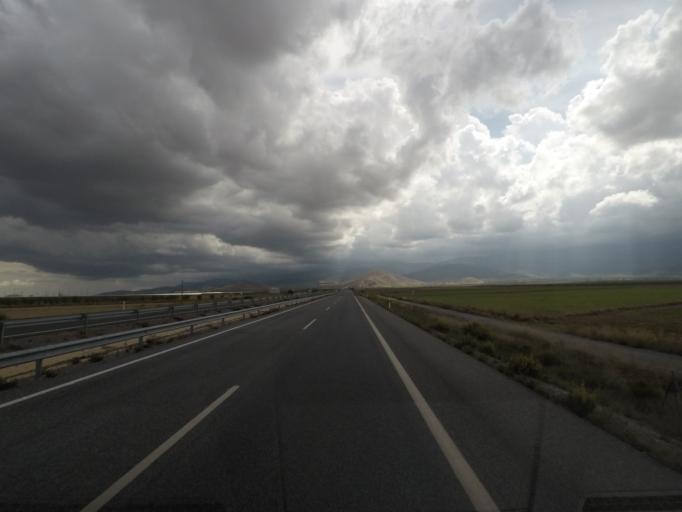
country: ES
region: Andalusia
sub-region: Provincia de Granada
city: Albunan
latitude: 37.2215
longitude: -3.0774
